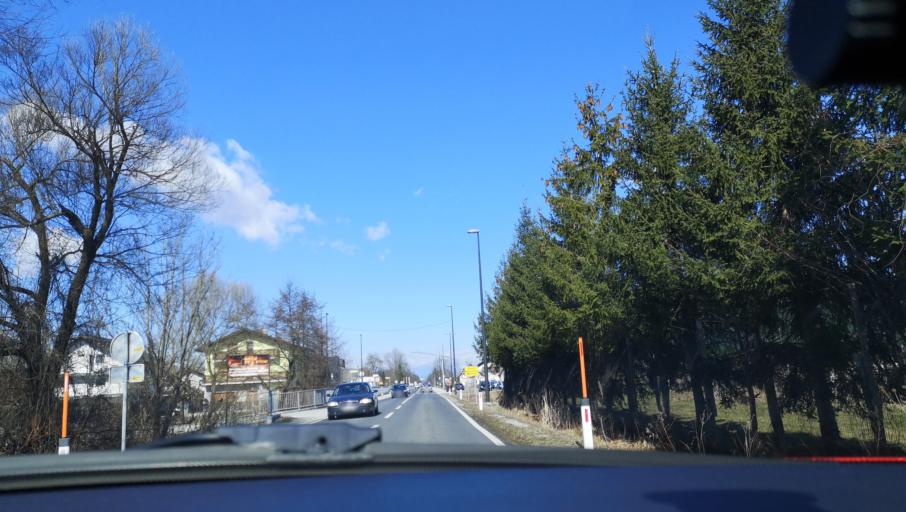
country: SI
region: Ig
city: Ig
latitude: 45.9984
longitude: 14.5173
